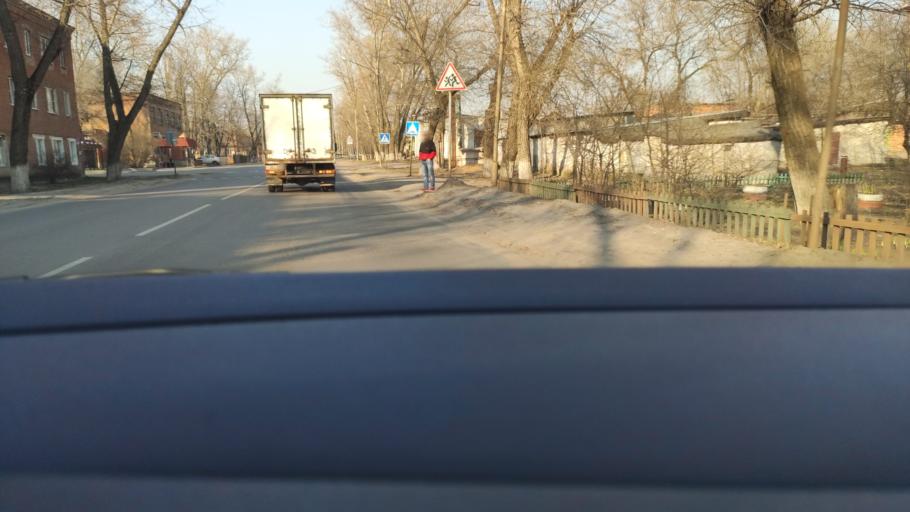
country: RU
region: Voronezj
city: Maslovka
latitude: 51.5804
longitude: 39.3155
